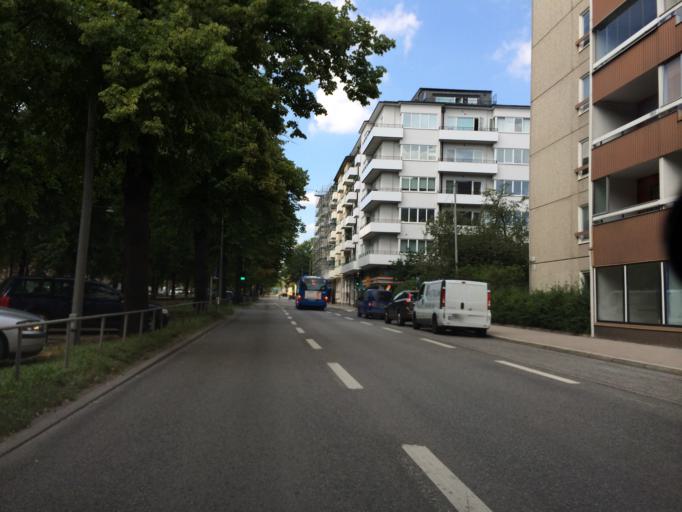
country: SE
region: Stockholm
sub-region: Stockholms Kommun
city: OEstermalm
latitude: 59.3416
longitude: 18.0881
